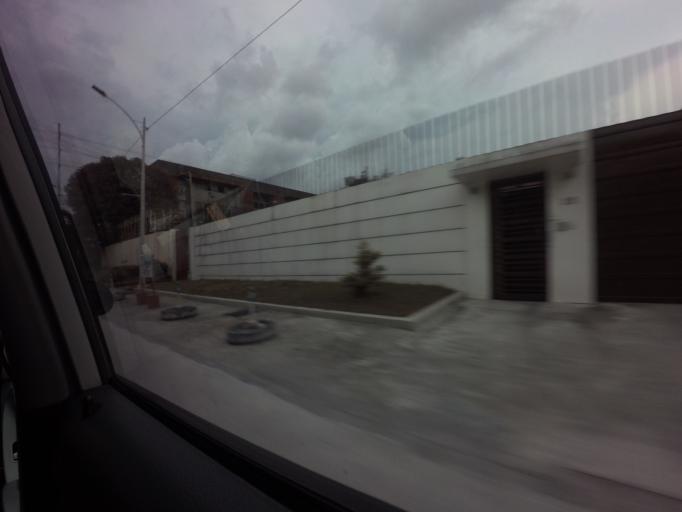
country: PH
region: Calabarzon
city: Del Monte
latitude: 14.6203
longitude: 121.0066
